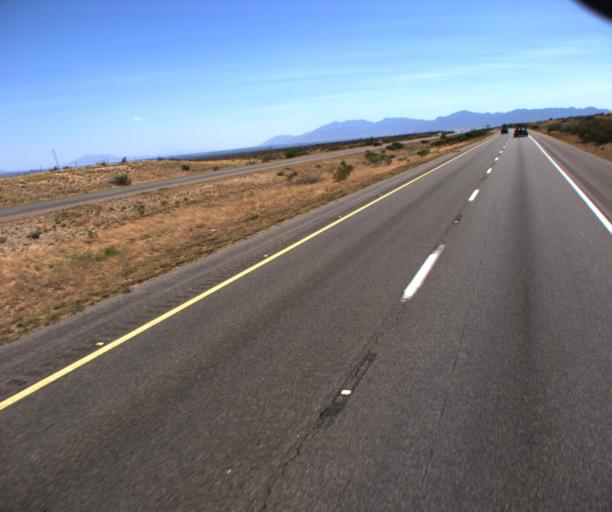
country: US
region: Arizona
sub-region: Cochise County
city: Whetstone
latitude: 31.8096
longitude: -110.3490
